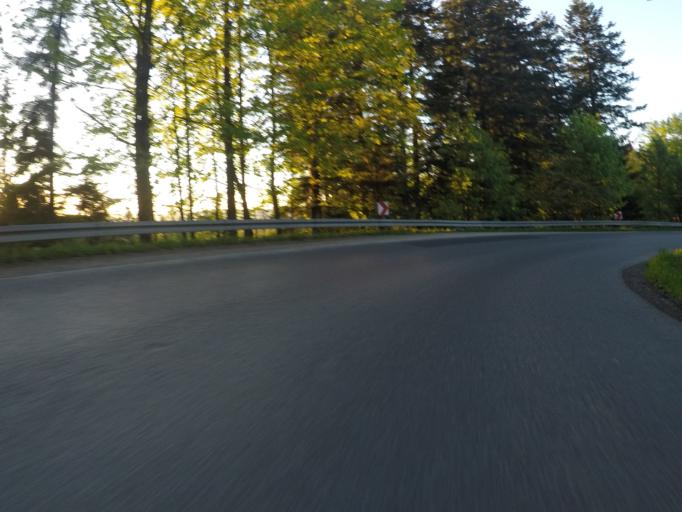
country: PL
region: Lesser Poland Voivodeship
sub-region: Powiat tatrzanski
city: Zakopane
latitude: 49.2830
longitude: 19.9990
